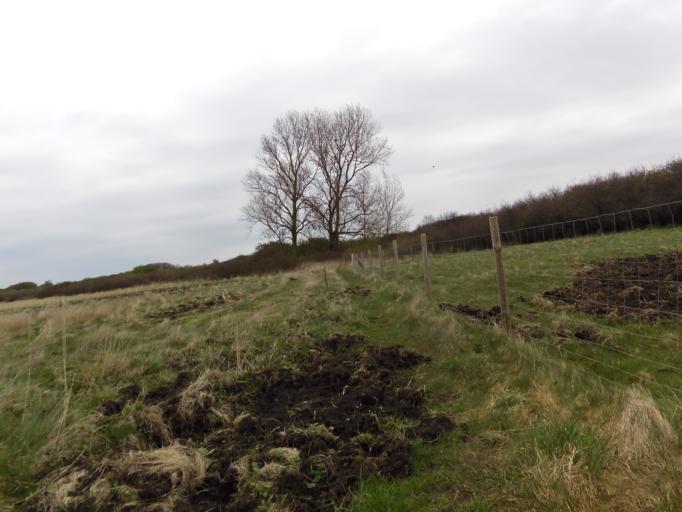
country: DE
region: Mecklenburg-Vorpommern
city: Hiddensee
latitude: 54.5995
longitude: 13.1417
